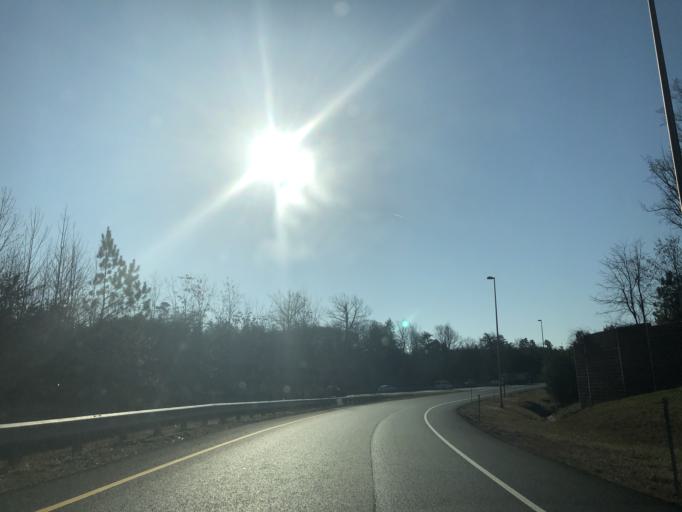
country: US
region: Virginia
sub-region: Stafford County
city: Falmouth
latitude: 38.3727
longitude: -77.4658
